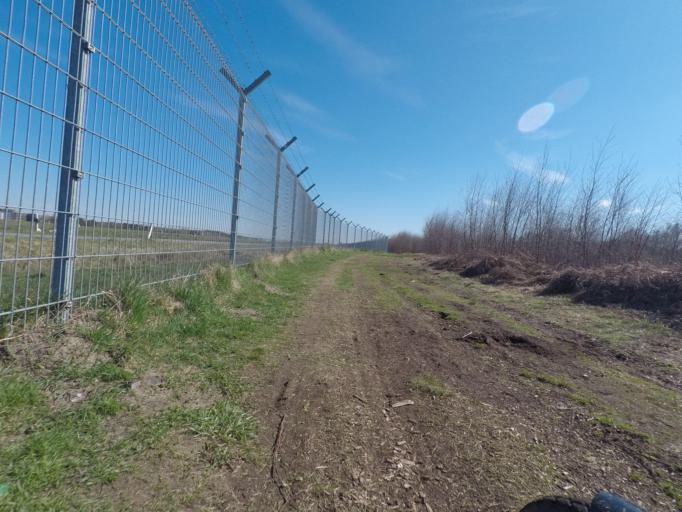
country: DE
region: Hamburg
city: Langenhorn
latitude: 53.6543
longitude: 9.9723
